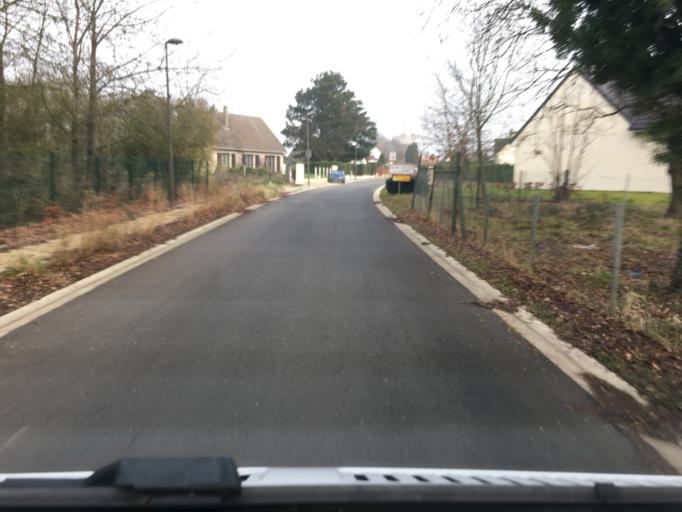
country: FR
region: Picardie
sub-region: Departement de la Somme
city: Saint-Valery-sur-Somme
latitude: 50.1775
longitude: 1.6300
